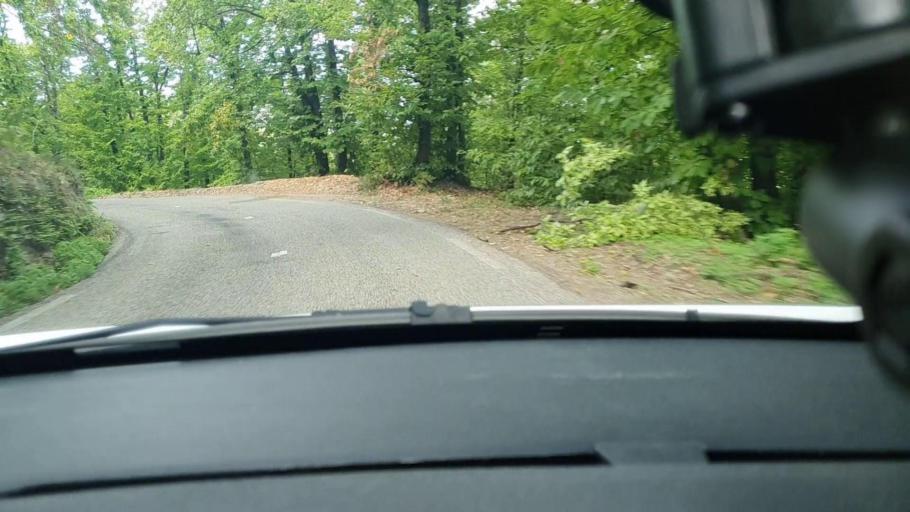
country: FR
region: Languedoc-Roussillon
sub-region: Departement du Gard
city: Branoux-les-Taillades
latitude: 44.2842
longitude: 3.9739
